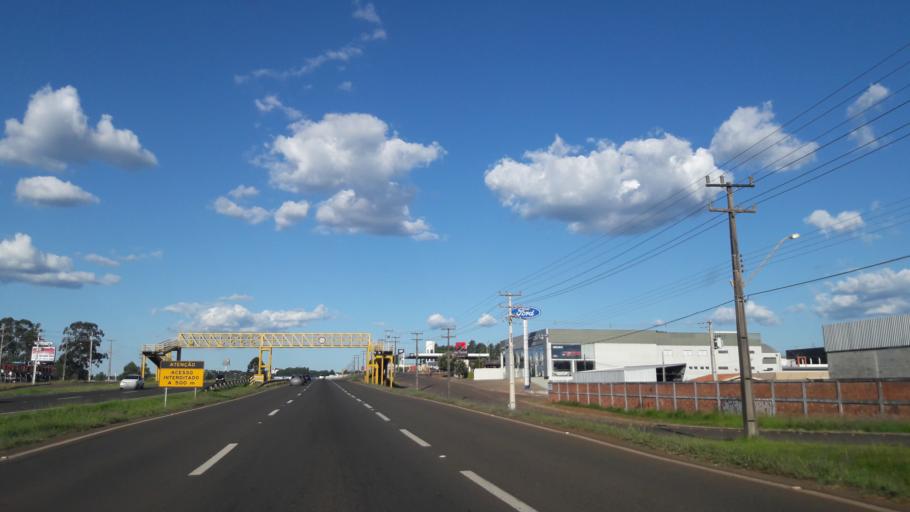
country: BR
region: Parana
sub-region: Guarapuava
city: Guarapuava
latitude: -25.3626
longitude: -51.4716
